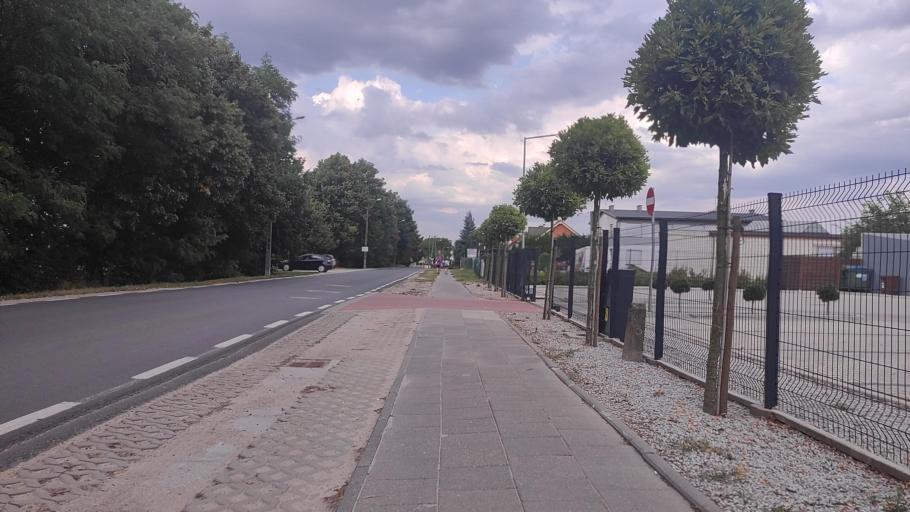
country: PL
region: Greater Poland Voivodeship
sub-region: Powiat poznanski
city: Swarzedz
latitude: 52.4234
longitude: 17.1003
